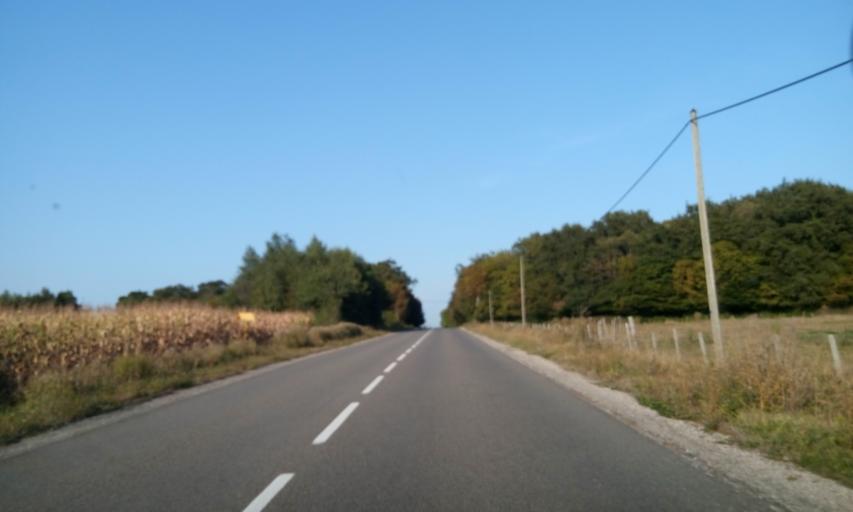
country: FR
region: Rhone-Alpes
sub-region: Departement de l'Ain
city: Chalamont
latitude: 46.0075
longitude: 5.1937
